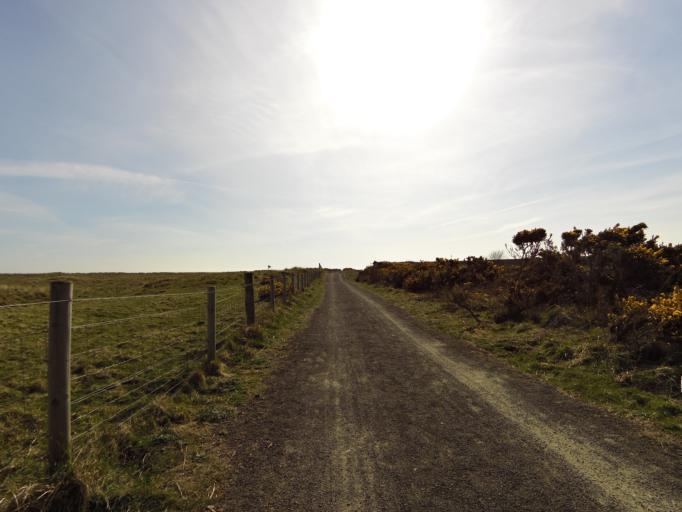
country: GB
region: Scotland
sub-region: Angus
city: Arbroath
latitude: 56.5292
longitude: -2.6370
